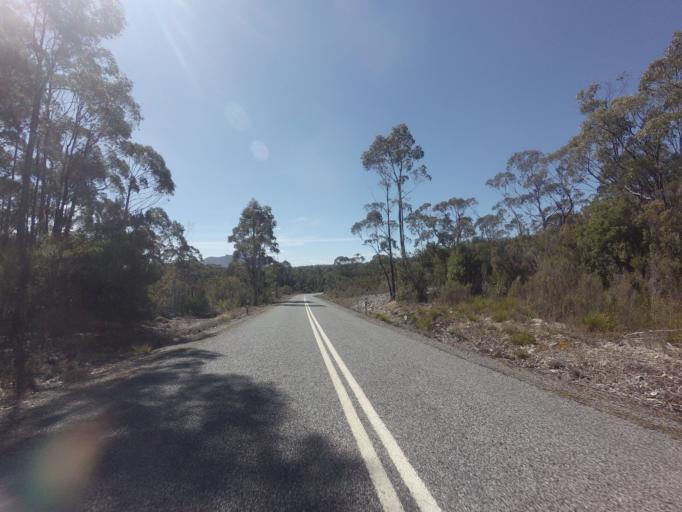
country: AU
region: Tasmania
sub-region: Huon Valley
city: Geeveston
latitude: -42.7713
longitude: 146.3968
